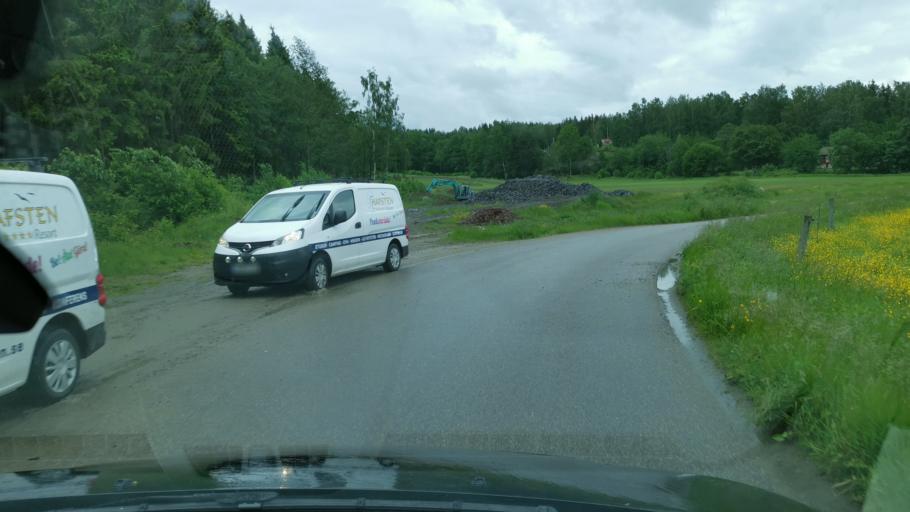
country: SE
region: Vaestra Goetaland
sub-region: Orust
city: Henan
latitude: 58.3221
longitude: 11.7174
